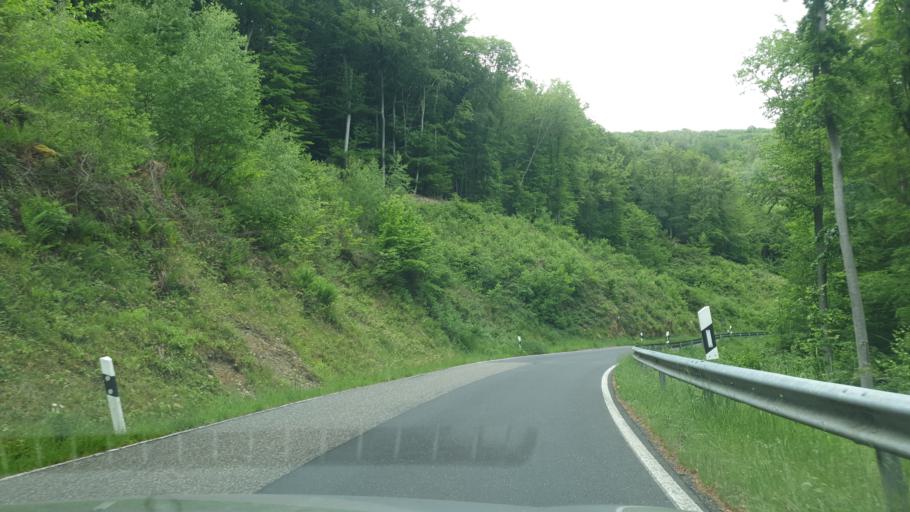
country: DE
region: Rheinland-Pfalz
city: Obernhof
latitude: 50.3311
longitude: 7.8501
